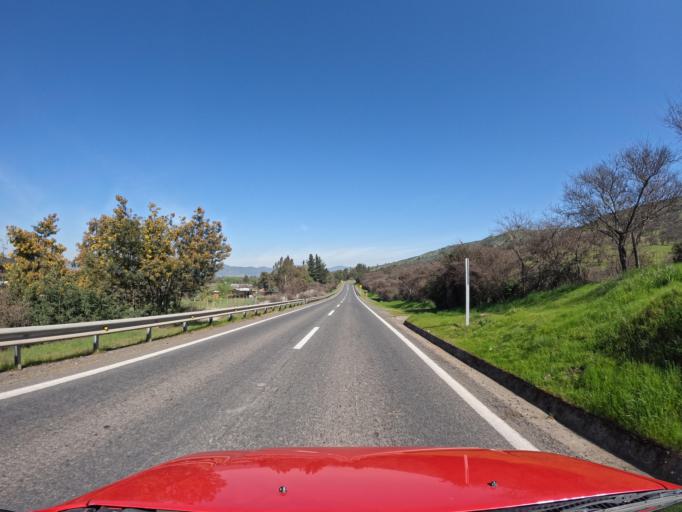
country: CL
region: Maule
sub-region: Provincia de Curico
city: Rauco
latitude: -35.0777
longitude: -71.6304
